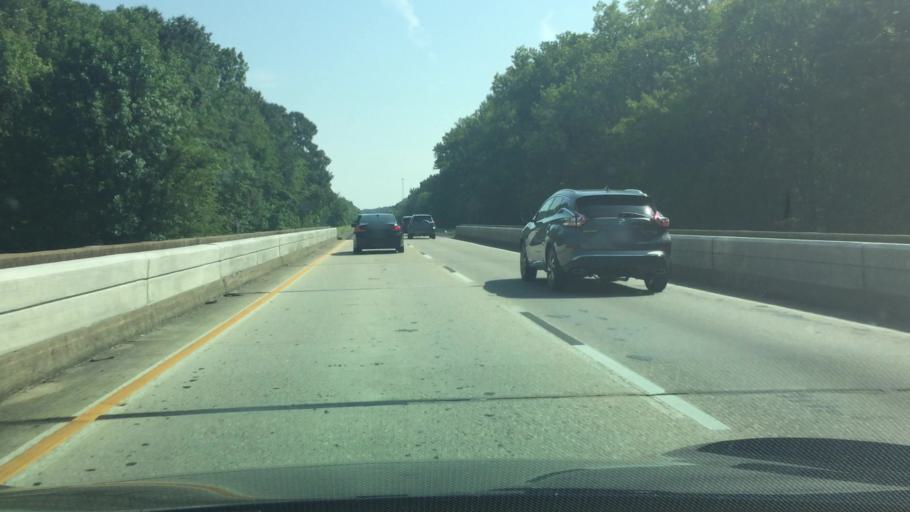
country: US
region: Alabama
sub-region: Montgomery County
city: Montgomery
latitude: 32.2217
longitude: -86.3947
